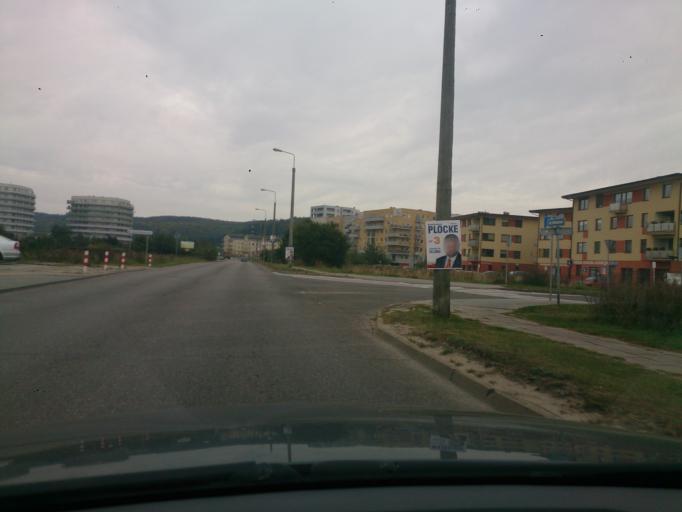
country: PL
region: Pomeranian Voivodeship
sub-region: Powiat wejherowski
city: Reda
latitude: 54.5975
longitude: 18.3630
